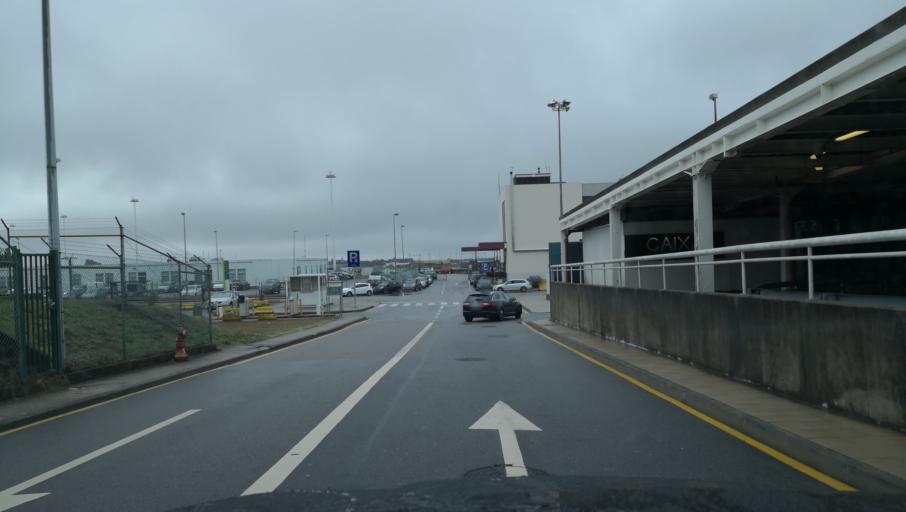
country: PT
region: Porto
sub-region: Matosinhos
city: Santa Cruz do Bispo
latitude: 41.2407
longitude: -8.6703
